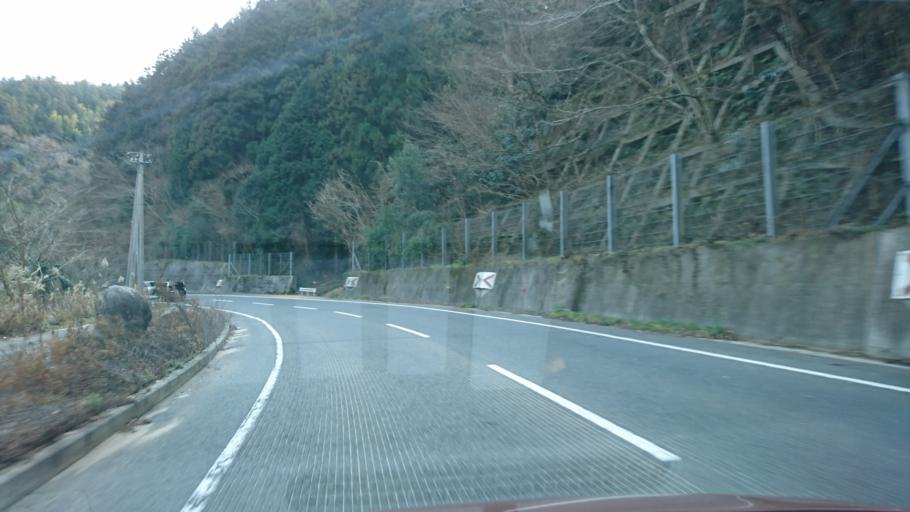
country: JP
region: Ehime
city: Hojo
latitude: 33.9165
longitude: 132.8828
